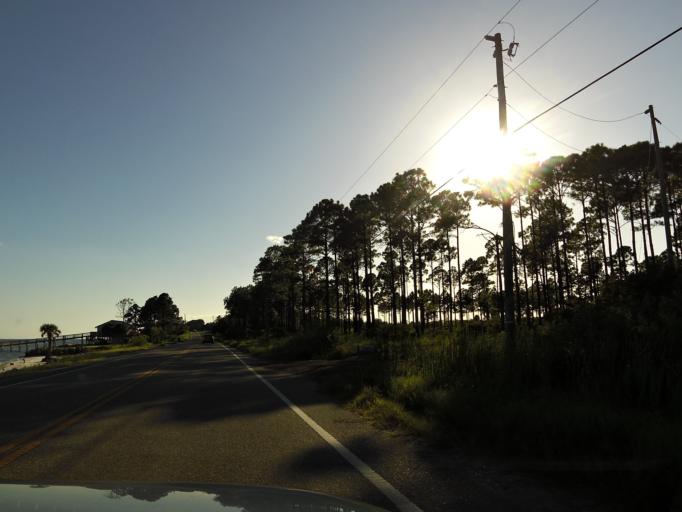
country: US
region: Florida
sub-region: Franklin County
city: Carrabelle
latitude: 29.8026
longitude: -84.7387
